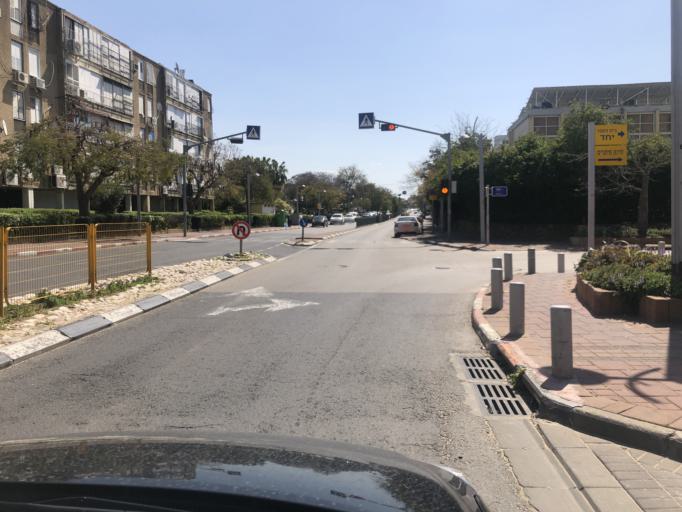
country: IL
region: Tel Aviv
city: Holon
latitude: 32.0135
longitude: 34.7649
